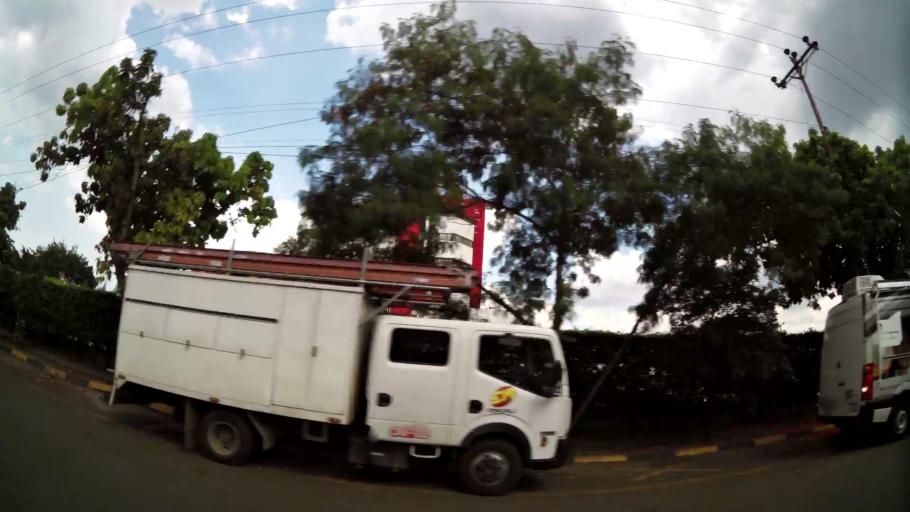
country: CO
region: Valle del Cauca
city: Cali
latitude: 3.4851
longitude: -76.4992
